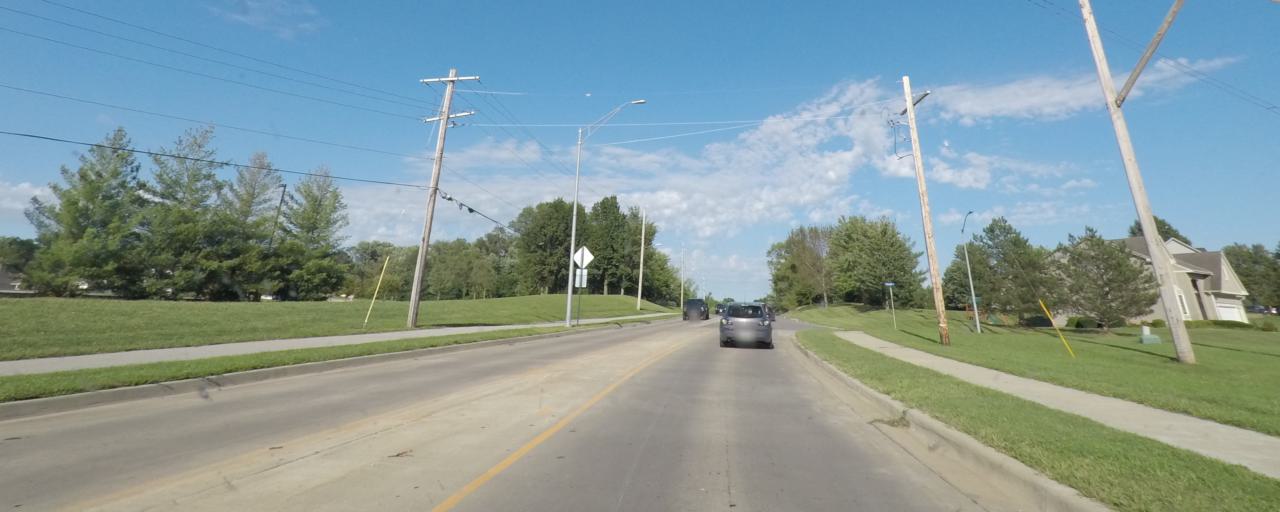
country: US
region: Missouri
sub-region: Clay County
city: Pleasant Valley
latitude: 39.2225
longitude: -94.4628
